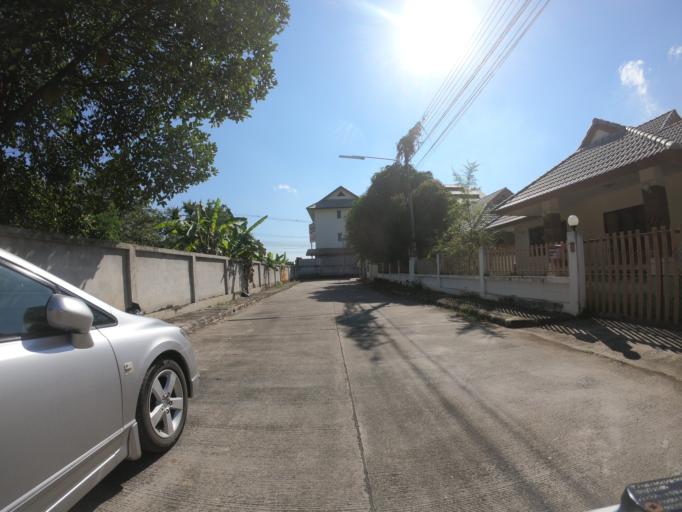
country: TH
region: Chiang Mai
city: Chiang Mai
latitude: 18.7459
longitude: 98.9793
